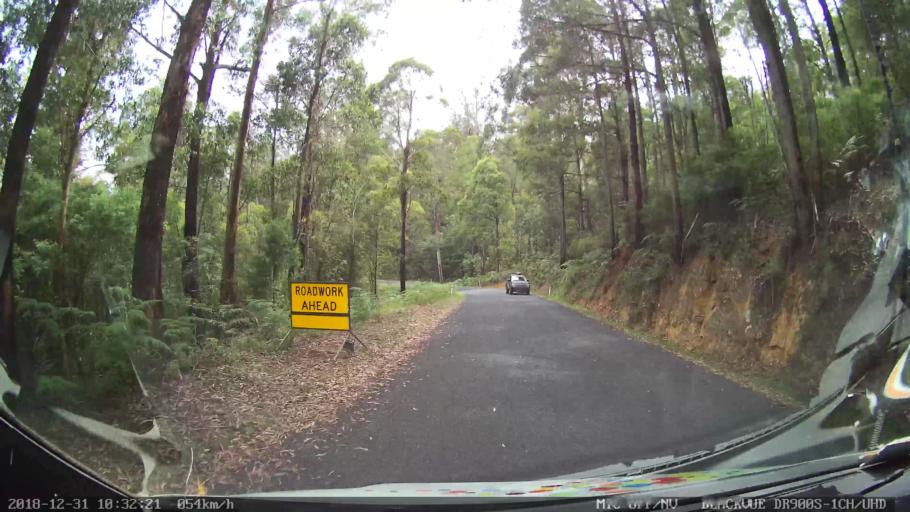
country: AU
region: New South Wales
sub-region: Snowy River
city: Jindabyne
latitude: -36.4512
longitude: 148.1604
